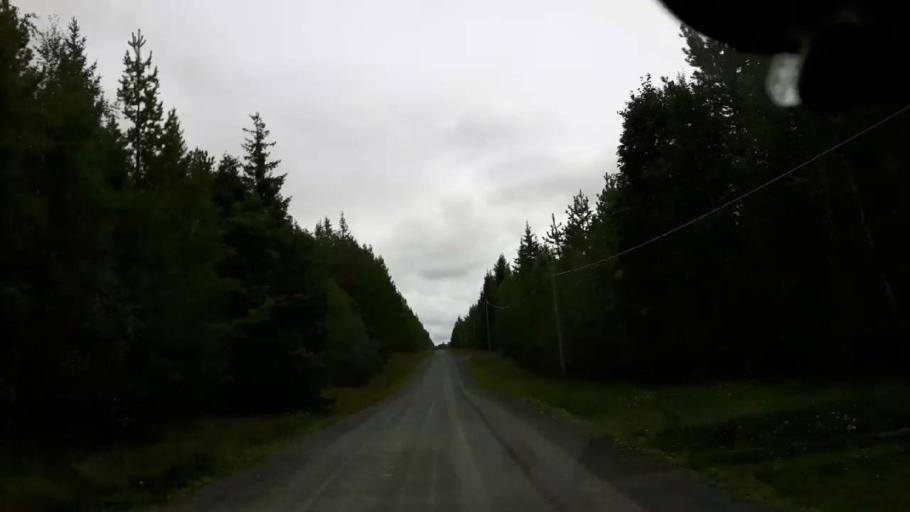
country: SE
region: Jaemtland
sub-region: Krokoms Kommun
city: Valla
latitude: 63.6879
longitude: 13.8955
